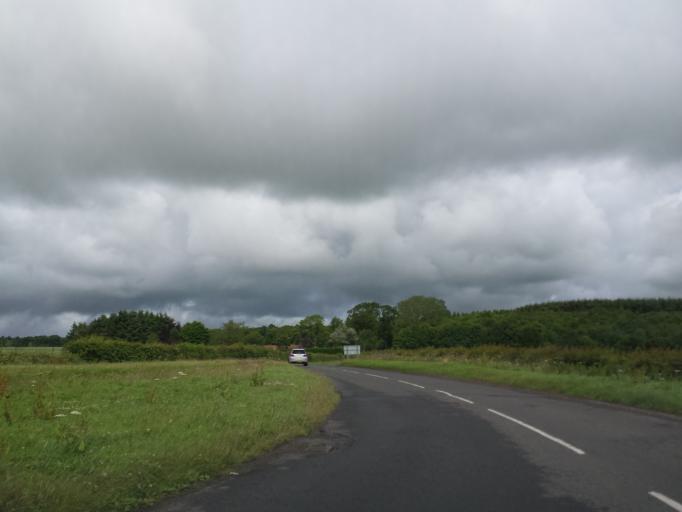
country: GB
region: Scotland
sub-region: Fife
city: Strathkinness
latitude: 56.3207
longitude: -2.8719
